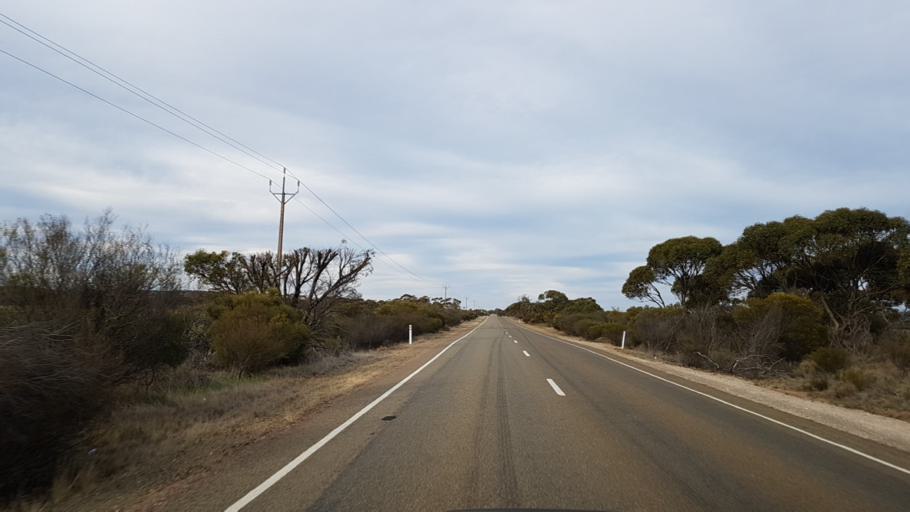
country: AU
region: South Australia
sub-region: Peterborough
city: Peterborough
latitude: -32.9867
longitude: 138.8005
